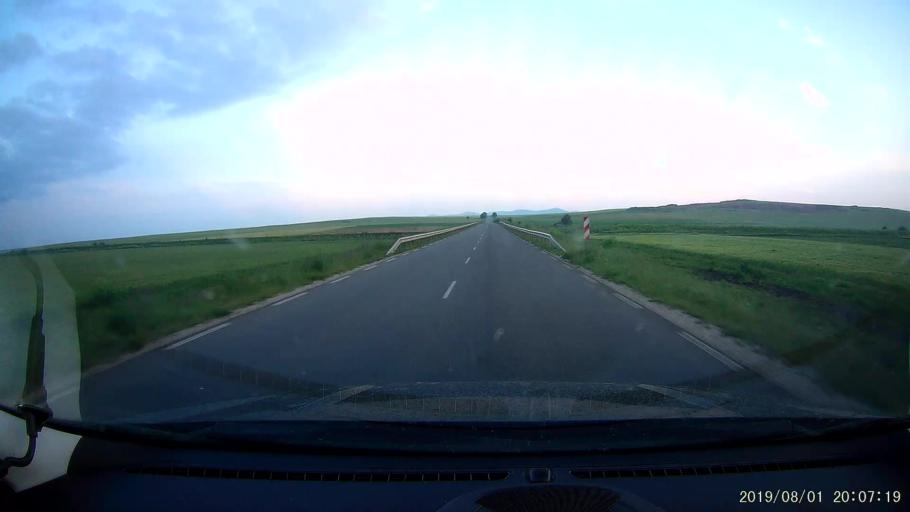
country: BG
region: Yambol
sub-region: Obshtina Yambol
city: Yambol
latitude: 42.5242
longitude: 26.5670
